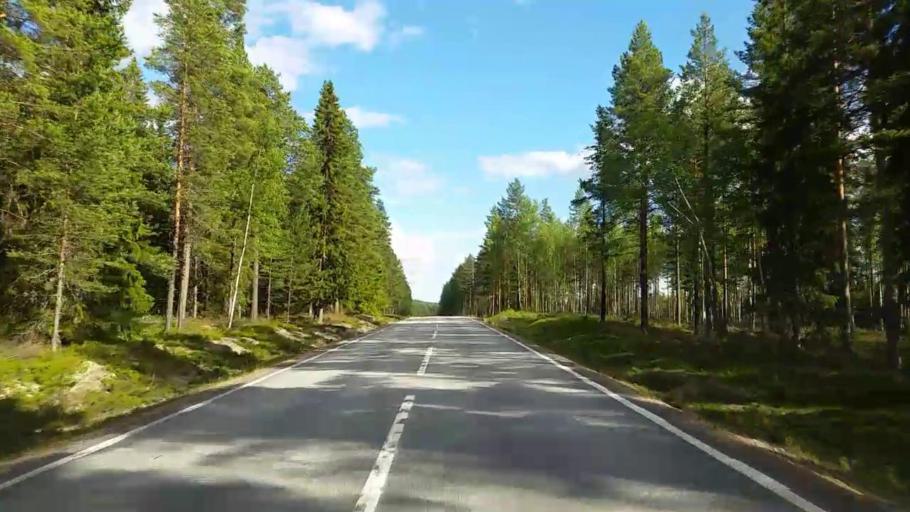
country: SE
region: Gaevleborg
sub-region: Ljusdals Kommun
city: Farila
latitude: 62.0910
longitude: 15.8022
